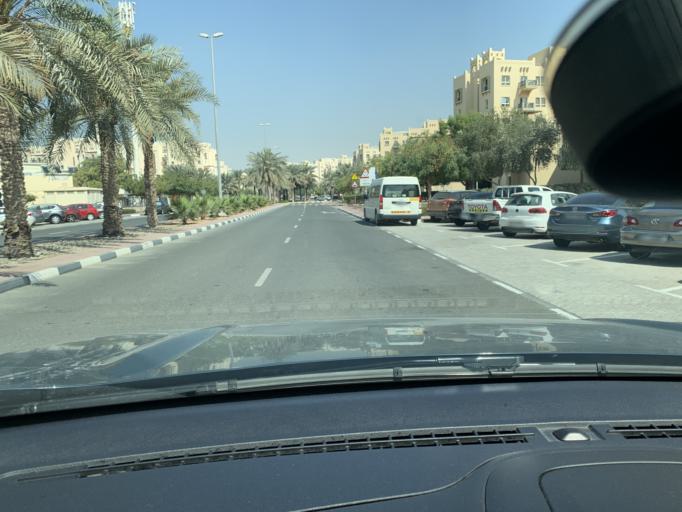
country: AE
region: Dubai
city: Dubai
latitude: 25.0044
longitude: 55.2492
